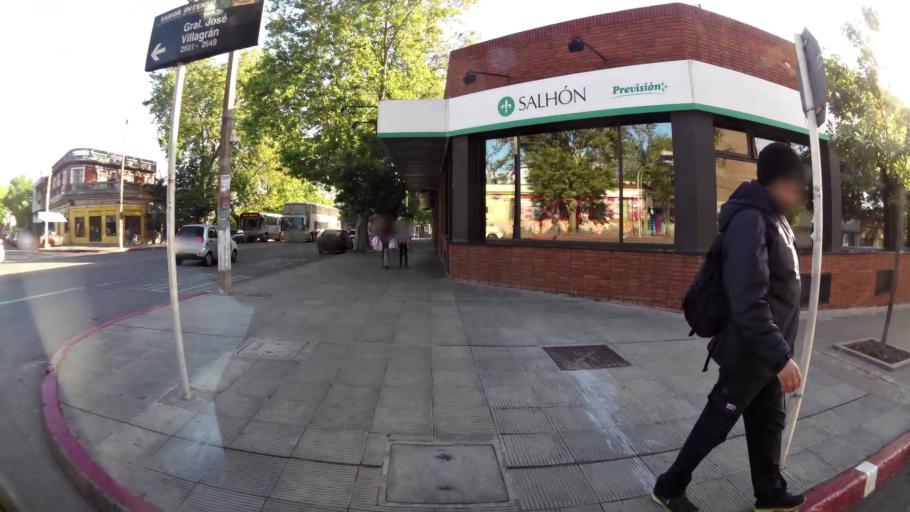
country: UY
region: Montevideo
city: Montevideo
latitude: -34.8686
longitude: -56.1348
